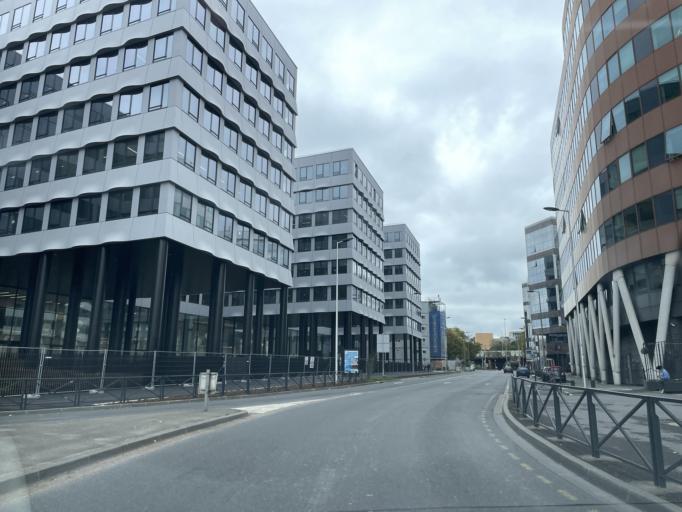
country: FR
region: Ile-de-France
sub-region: Departement du Val-de-Marne
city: Le Perreux-sur-Marne
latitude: 48.8538
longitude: 2.4930
